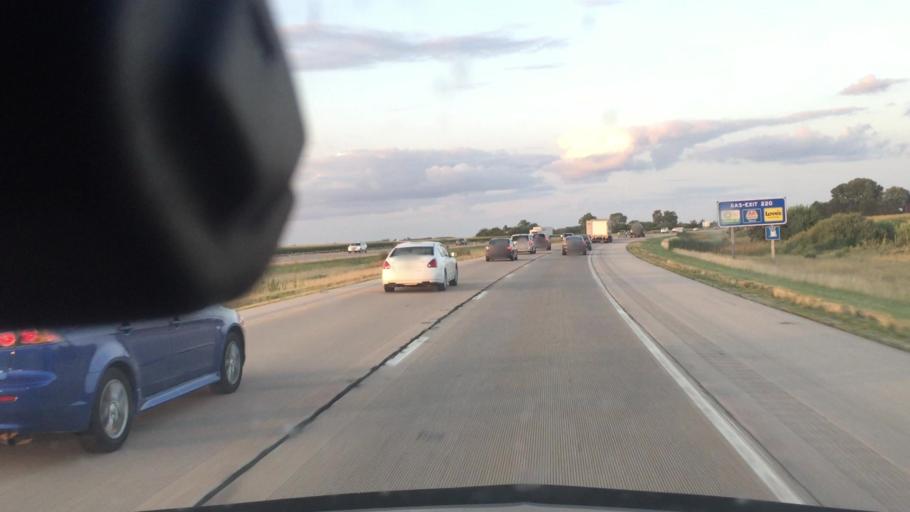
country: US
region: Illinois
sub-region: Livingston County
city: Dwight
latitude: 41.1112
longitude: -88.4431
